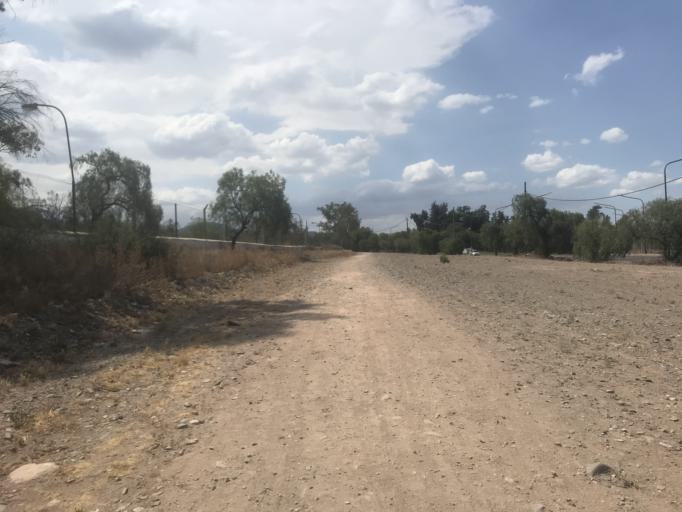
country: AR
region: Mendoza
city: Mendoza
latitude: -32.8860
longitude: -68.8849
